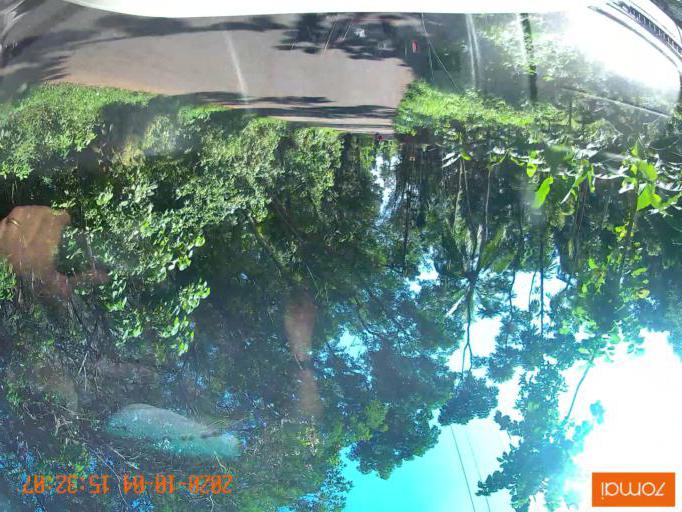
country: IN
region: Kerala
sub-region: Kottayam
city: Palackattumala
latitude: 9.7334
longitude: 76.6361
